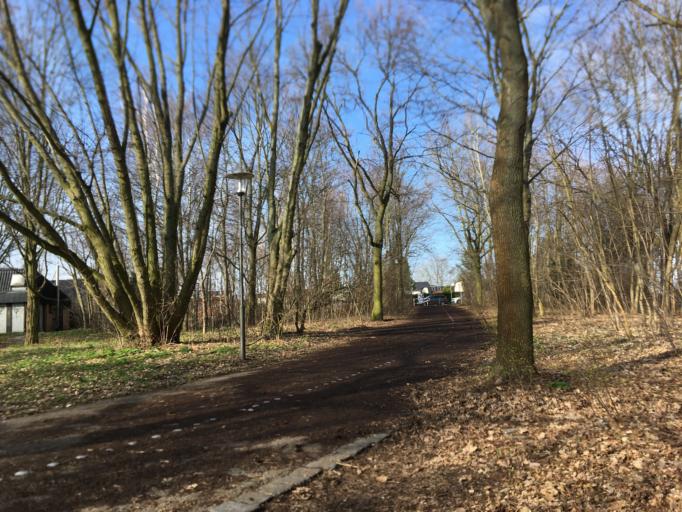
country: DE
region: Berlin
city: Rosenthal
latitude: 52.6138
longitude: 13.3699
